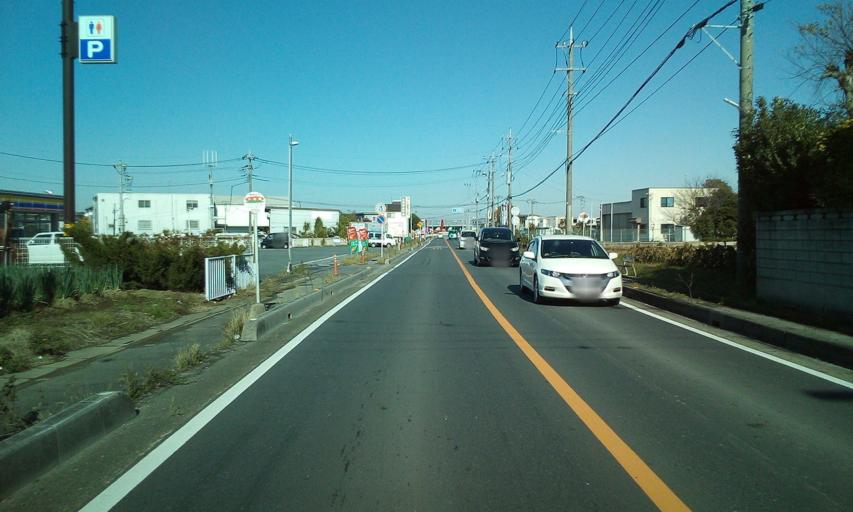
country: JP
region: Chiba
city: Nagareyama
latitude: 35.8654
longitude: 139.8881
